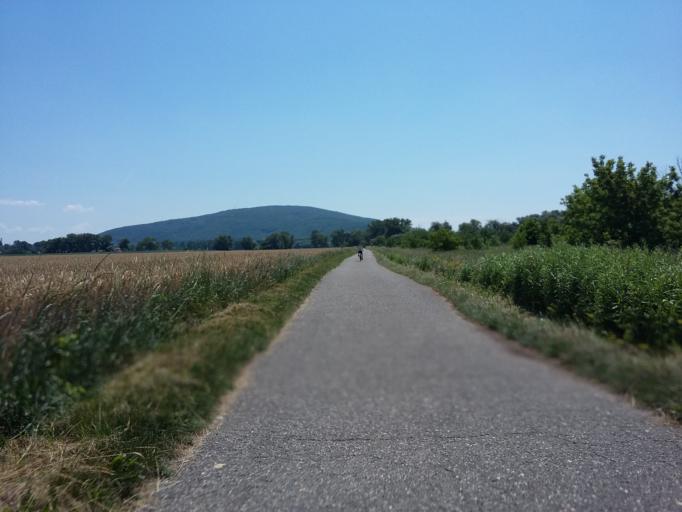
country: AT
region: Lower Austria
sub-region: Politischer Bezirk Ganserndorf
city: Marchegg
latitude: 48.2290
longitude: 16.9574
